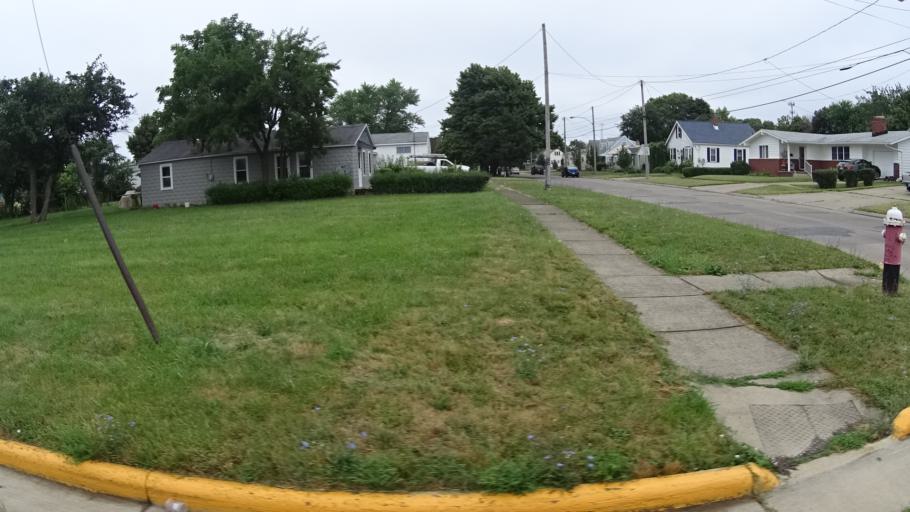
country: US
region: Ohio
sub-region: Erie County
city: Sandusky
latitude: 41.4402
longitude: -82.7004
